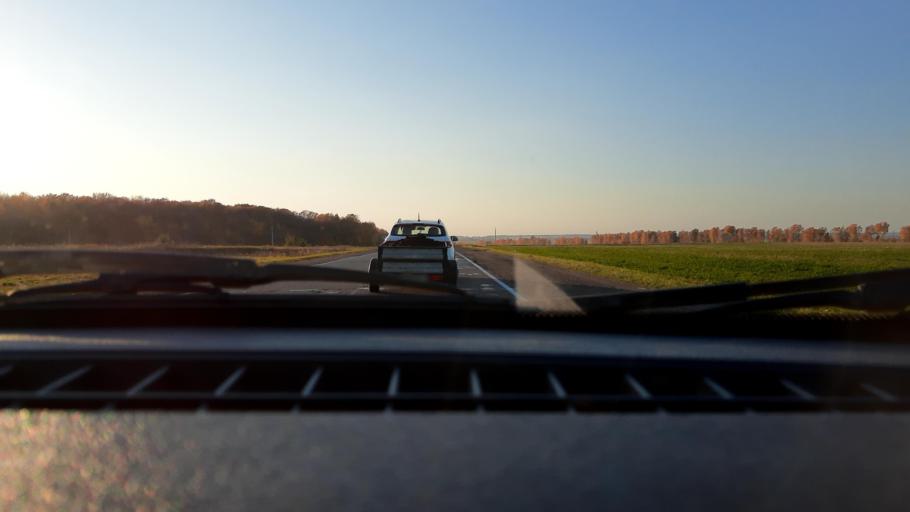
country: RU
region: Bashkortostan
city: Asanovo
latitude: 54.8249
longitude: 55.6477
